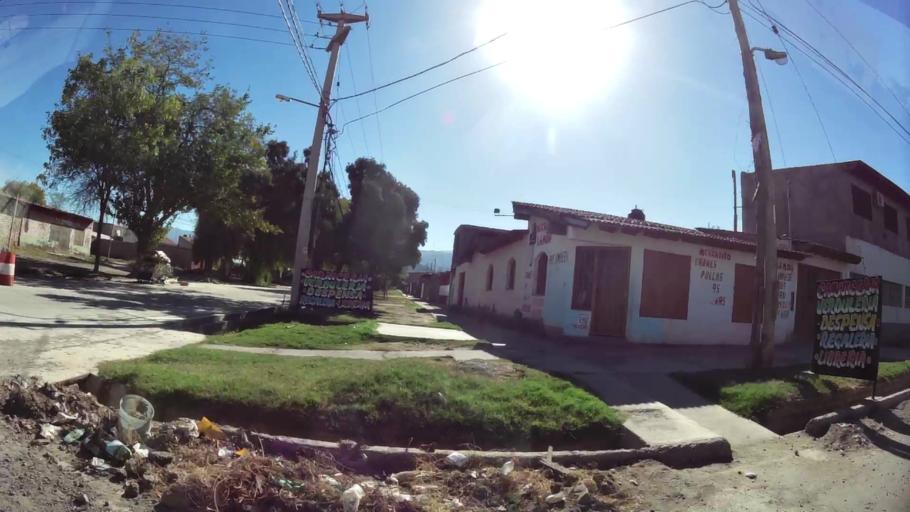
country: AR
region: Mendoza
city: Las Heras
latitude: -32.8323
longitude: -68.8291
